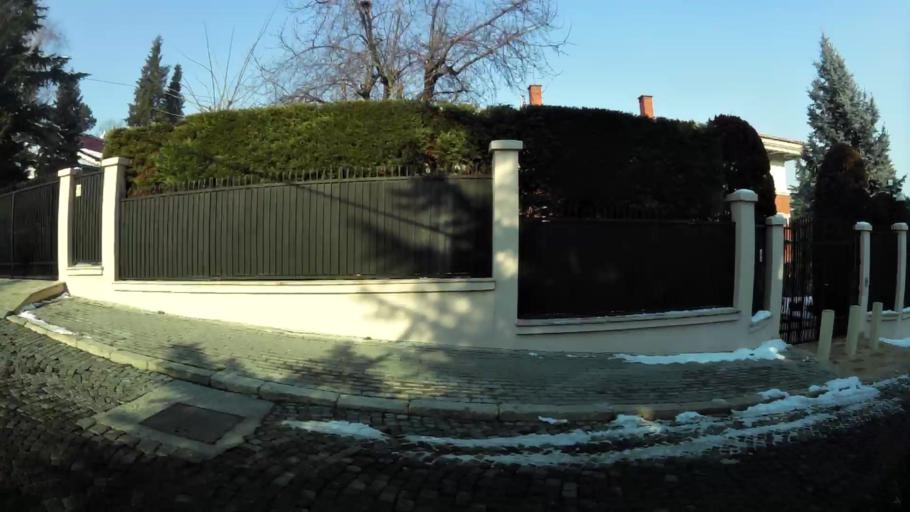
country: MK
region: Karpos
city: Skopje
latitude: 41.9877
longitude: 21.4149
